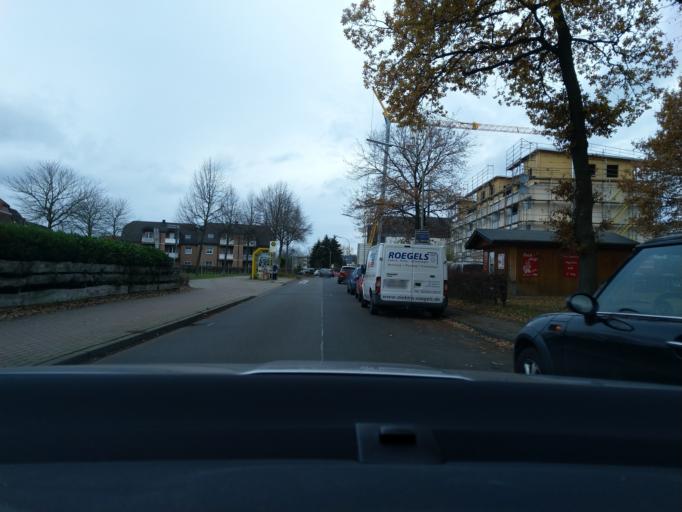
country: DE
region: North Rhine-Westphalia
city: Wegberg
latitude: 51.1393
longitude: 6.2998
